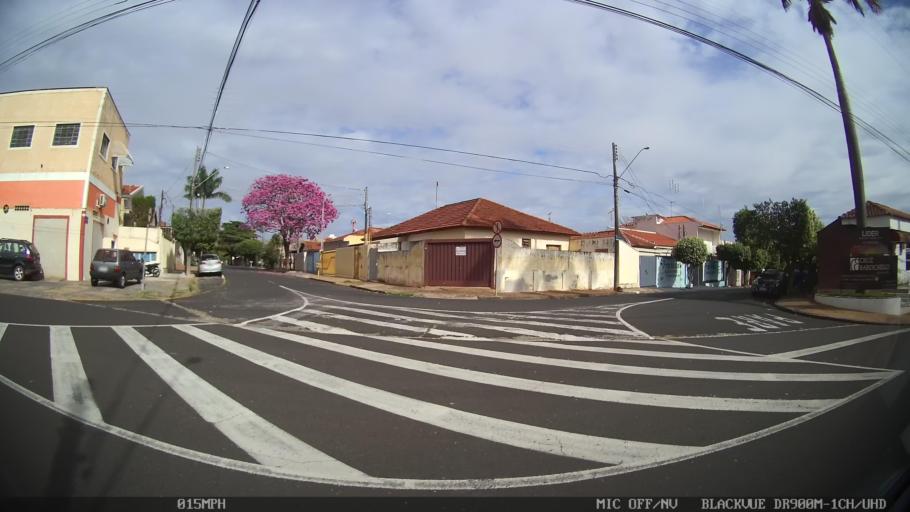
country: BR
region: Sao Paulo
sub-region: Sao Jose Do Rio Preto
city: Sao Jose do Rio Preto
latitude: -20.8216
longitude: -49.3750
